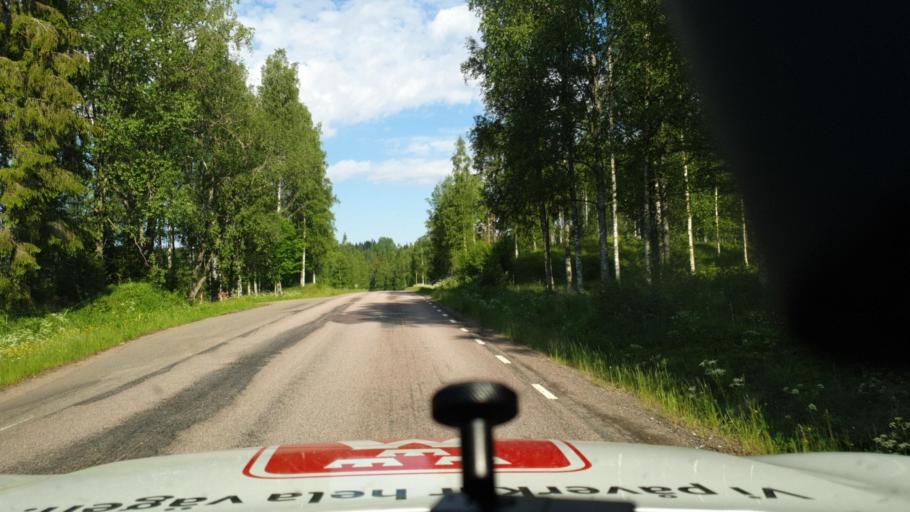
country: SE
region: Vaermland
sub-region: Arvika Kommun
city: Arvika
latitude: 59.9547
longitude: 12.7239
